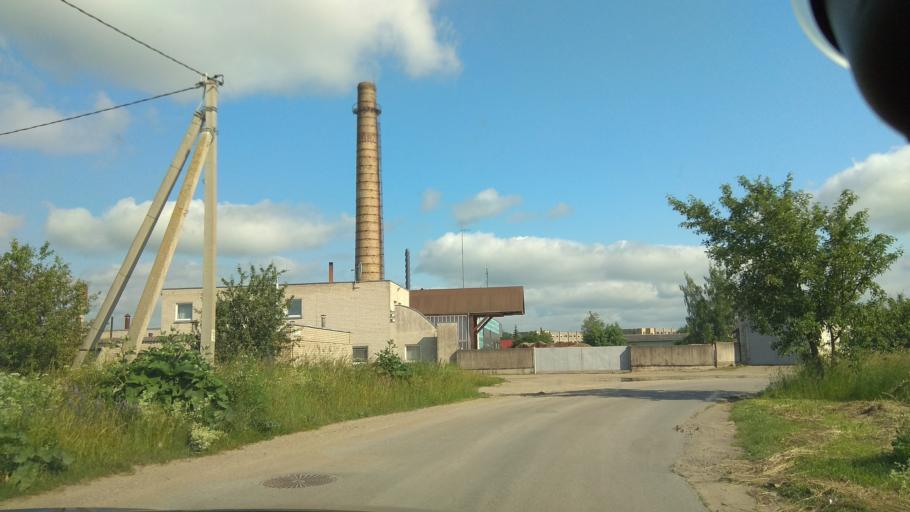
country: LT
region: Siauliu apskritis
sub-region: Joniskis
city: Joniskis
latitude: 56.2441
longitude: 23.6276
